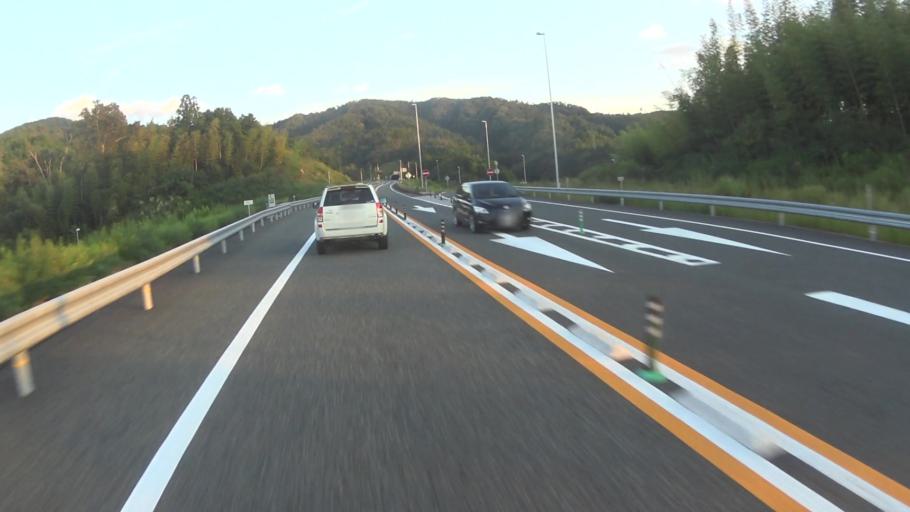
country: JP
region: Kyoto
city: Ayabe
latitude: 35.3370
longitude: 135.3081
